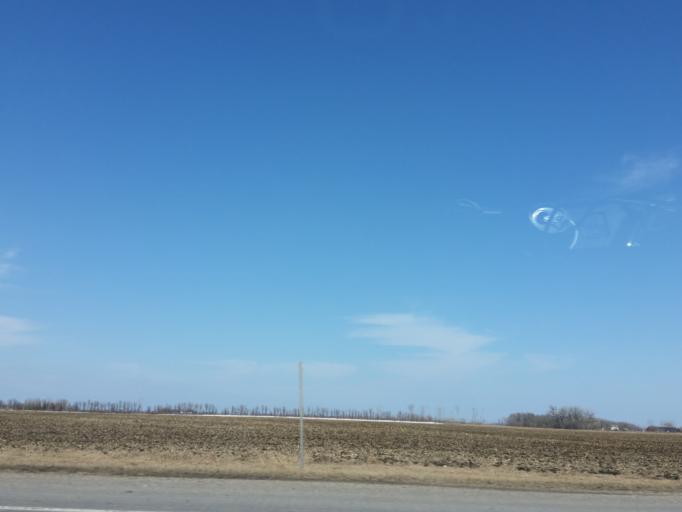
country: US
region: North Dakota
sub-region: Walsh County
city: Grafton
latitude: 48.2099
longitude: -97.3451
